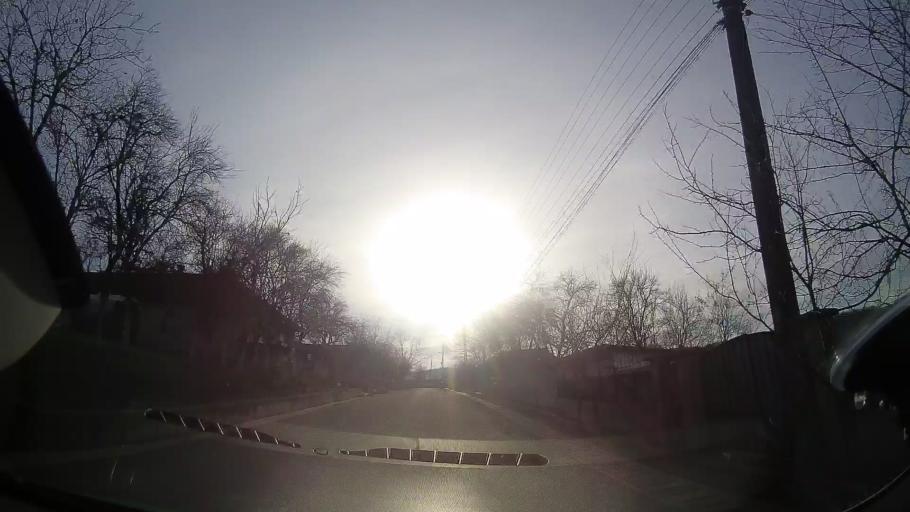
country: RO
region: Bihor
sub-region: Comuna Sarbi
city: Burzuc
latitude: 47.1425
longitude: 22.1850
